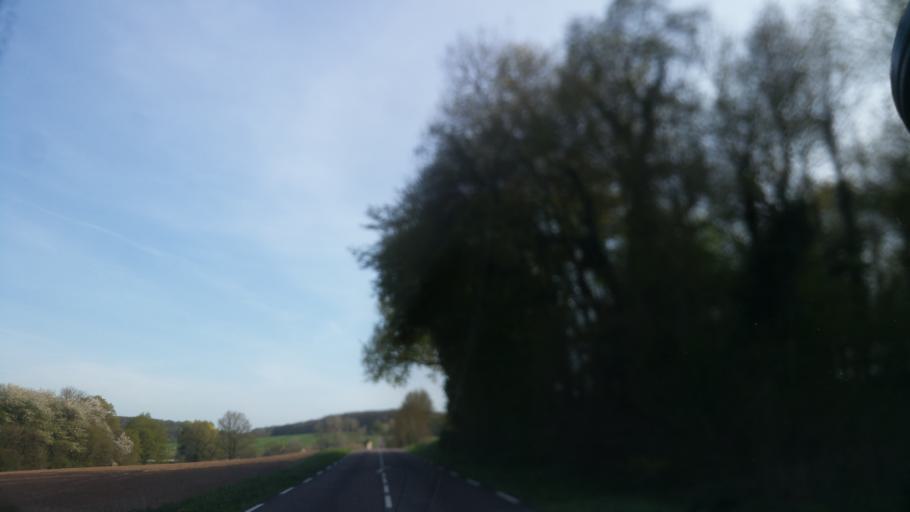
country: FR
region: Ile-de-France
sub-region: Departement de l'Essonne
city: Saint-Cyr-sous-Dourdan
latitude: 48.5620
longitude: 2.0285
